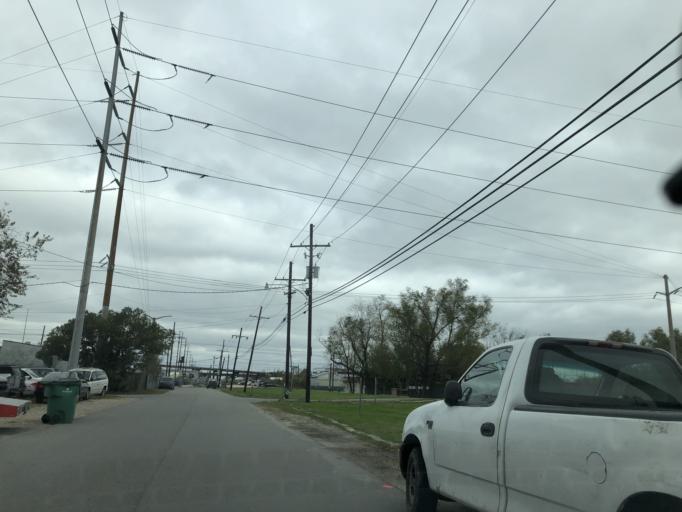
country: US
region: Louisiana
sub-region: Jefferson Parish
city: Metairie Terrace
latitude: 29.9744
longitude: -90.1624
